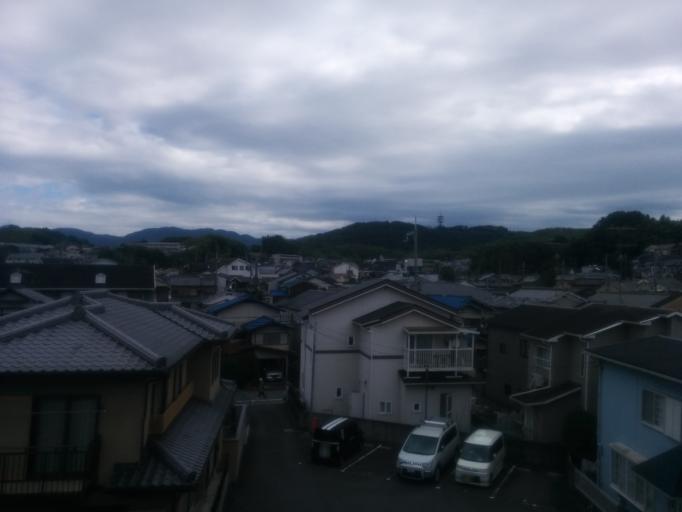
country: JP
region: Kyoto
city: Uji
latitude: 34.9553
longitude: 135.7775
